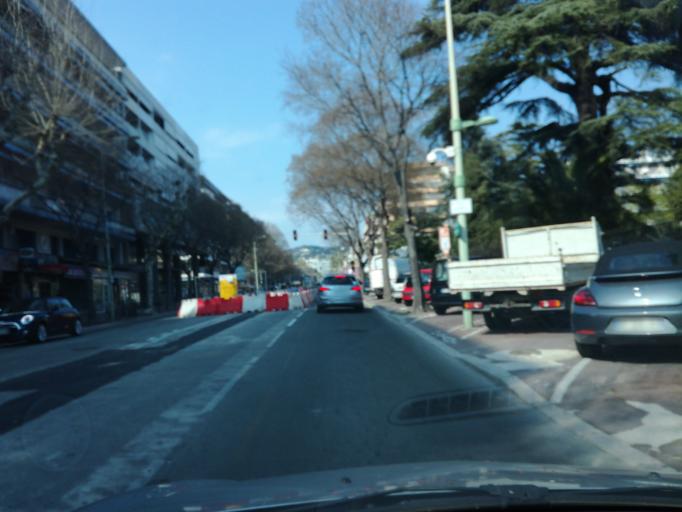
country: FR
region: Provence-Alpes-Cote d'Azur
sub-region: Departement des Alpes-Maritimes
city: Le Cannet
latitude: 43.5648
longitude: 7.0167
